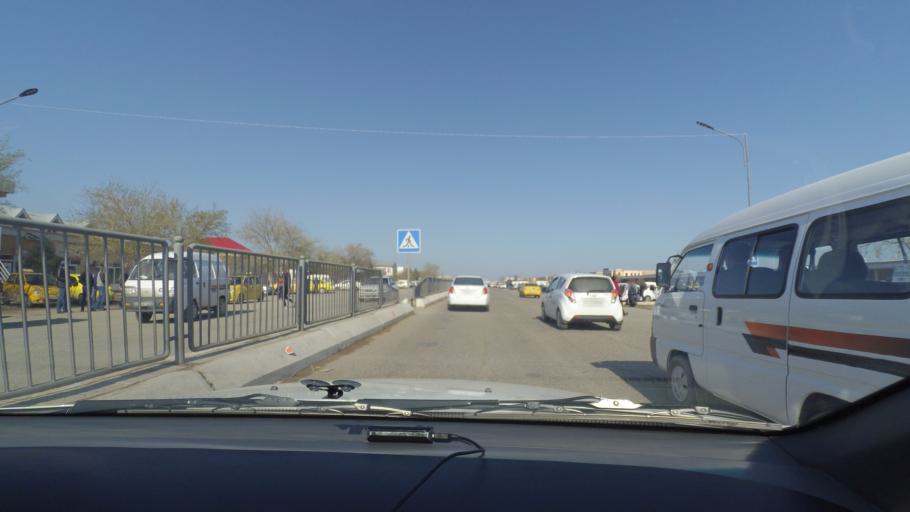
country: UZ
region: Bukhara
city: Bukhara
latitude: 39.8046
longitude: 64.4255
